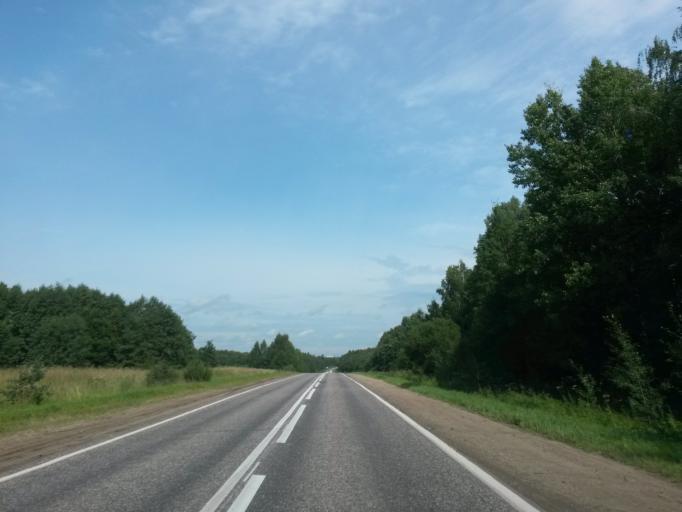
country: RU
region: Jaroslavl
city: Krasnyye Tkachi
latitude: 57.4823
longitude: 39.9043
